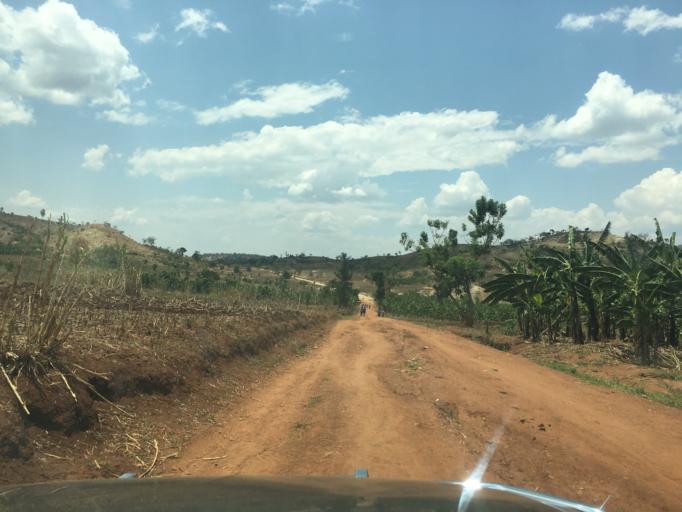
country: RW
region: Eastern Province
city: Kibungo
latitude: -2.1289
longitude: 30.8528
